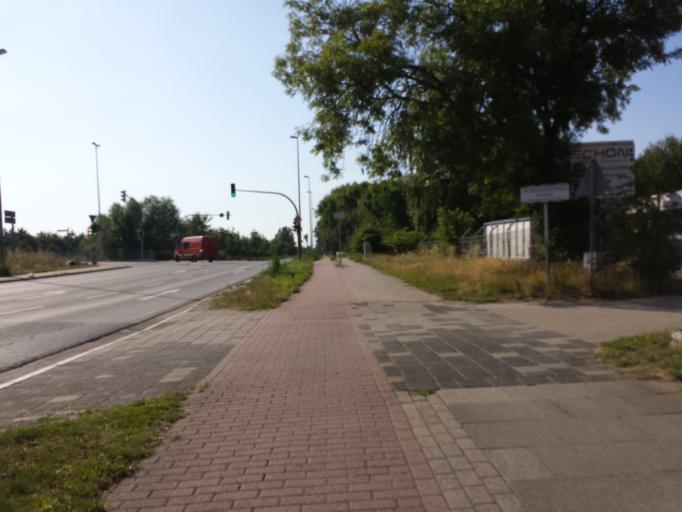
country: DE
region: Bremen
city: Bremen
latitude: 53.0721
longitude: 8.7711
